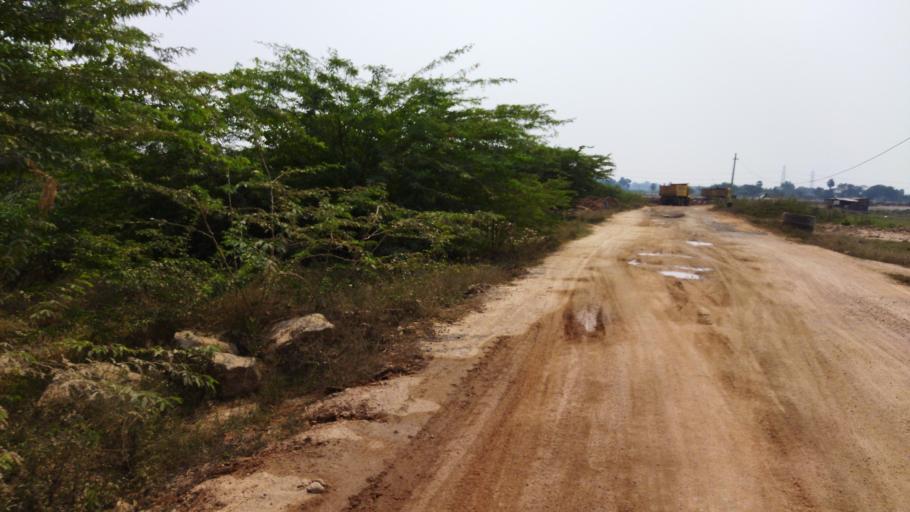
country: IN
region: Telangana
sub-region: Nalgonda
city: Nalgonda
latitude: 17.1388
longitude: 79.3857
